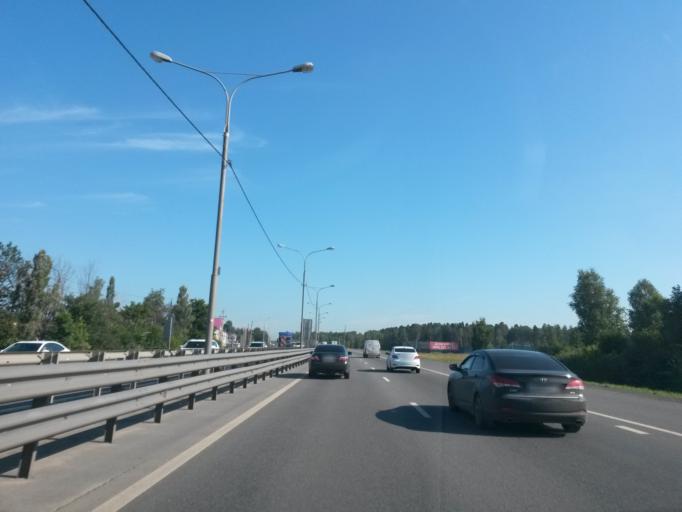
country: RU
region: Moskovskaya
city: Pushkino
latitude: 56.0006
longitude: 37.8775
